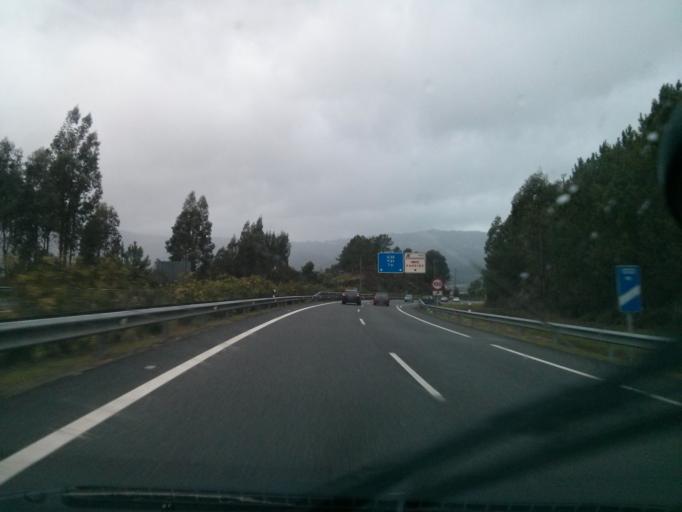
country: ES
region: Galicia
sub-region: Provincia de Pontevedra
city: Porrino
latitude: 42.1599
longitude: -8.6051
